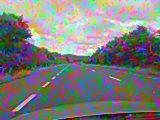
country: IE
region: Ulster
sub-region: County Donegal
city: Donegal
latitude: 54.6896
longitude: -8.0134
